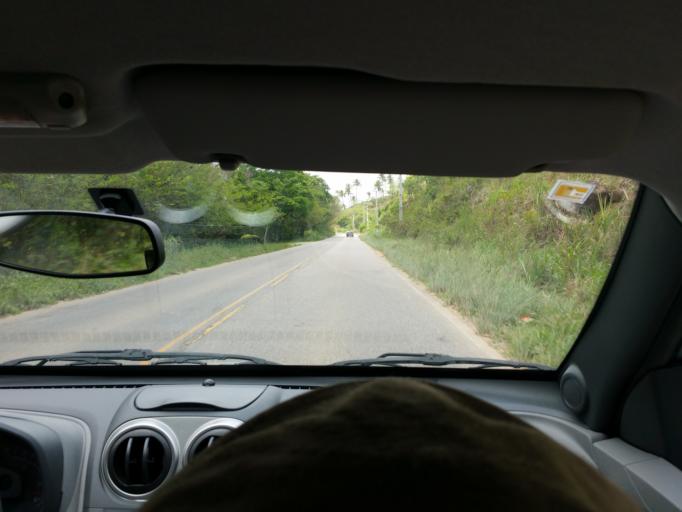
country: BR
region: Pernambuco
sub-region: Sirinhaem
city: Sirinhaem
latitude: -8.6306
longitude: -35.1206
